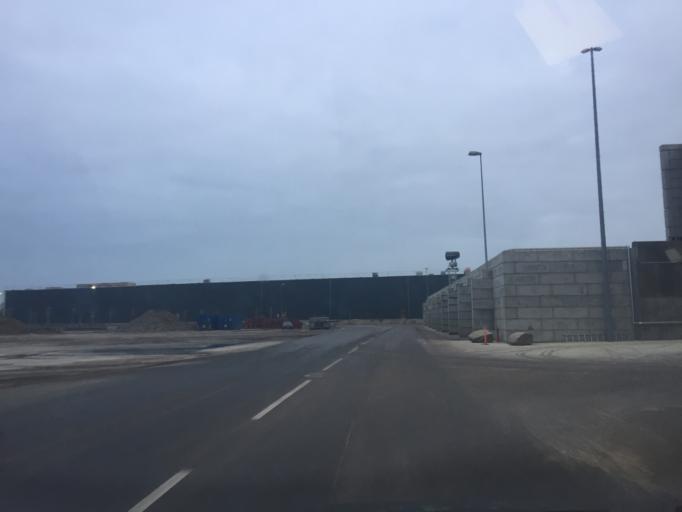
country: DK
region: Zealand
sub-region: Koge Kommune
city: Koge
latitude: 55.4633
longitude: 12.1918
